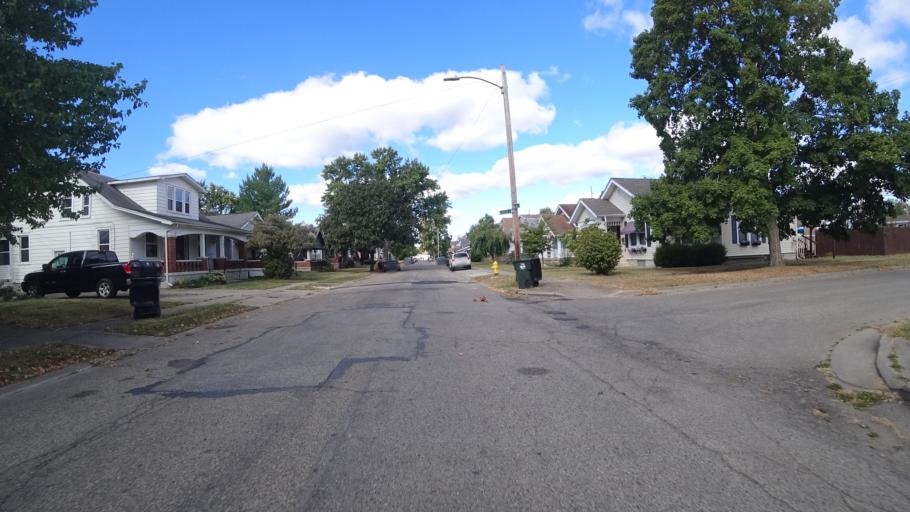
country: US
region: Ohio
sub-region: Butler County
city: Fairfield
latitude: 39.3669
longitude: -84.5542
